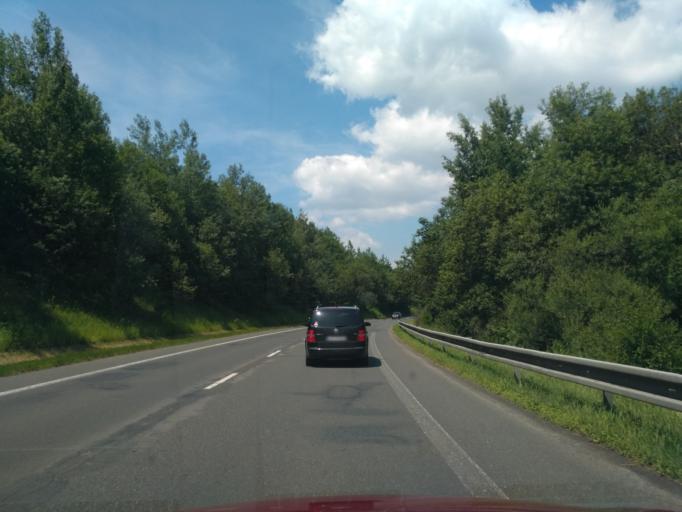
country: SK
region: Presovsky
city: Stara L'ubovna
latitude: 49.2979
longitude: 20.7095
